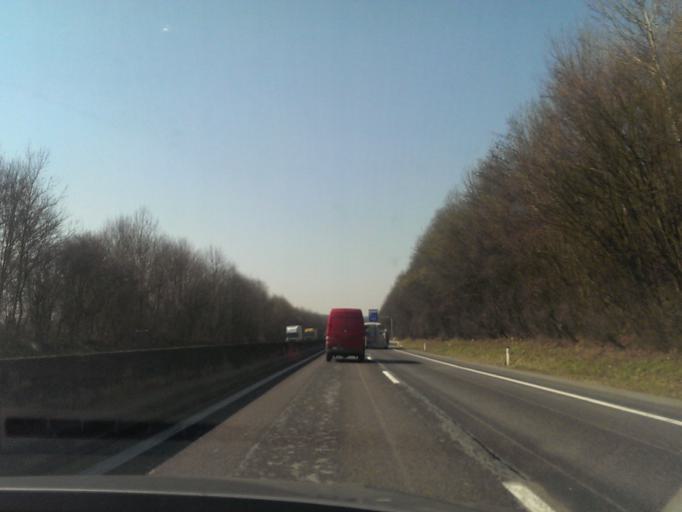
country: AT
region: Upper Austria
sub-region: Politischer Bezirk Ried im Innkreis
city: Ried im Innkreis
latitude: 48.2419
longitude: 13.5471
